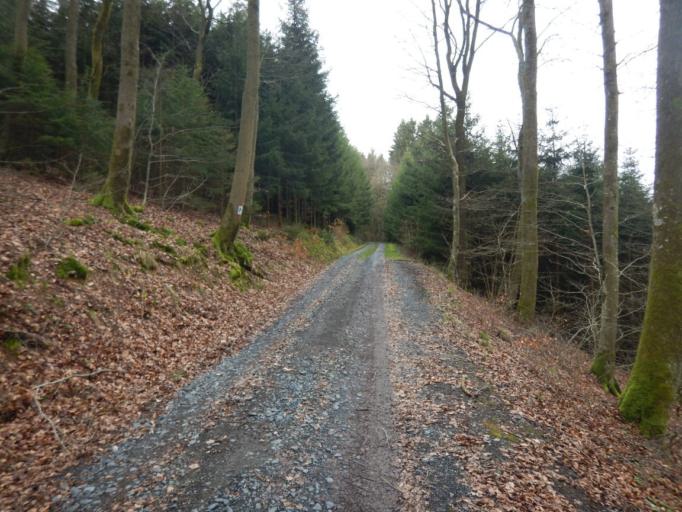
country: LU
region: Diekirch
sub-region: Canton de Wiltz
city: Esch-sur-Sure
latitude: 49.9290
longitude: 5.9093
